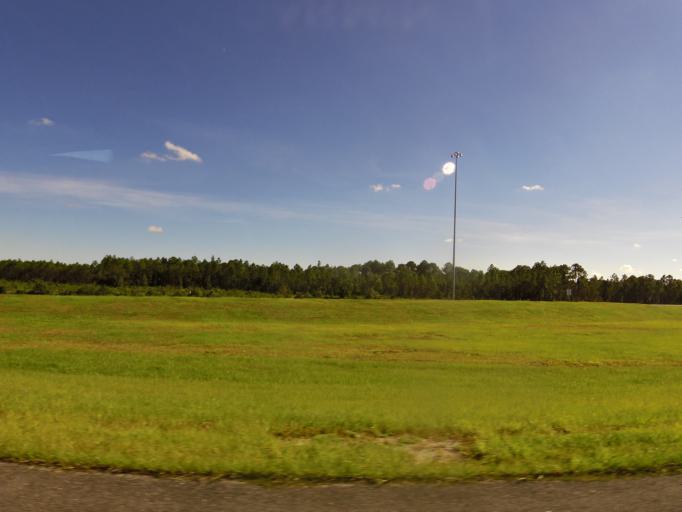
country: US
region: Florida
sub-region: Saint Johns County
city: Palm Valley
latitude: 30.1122
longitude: -81.4427
